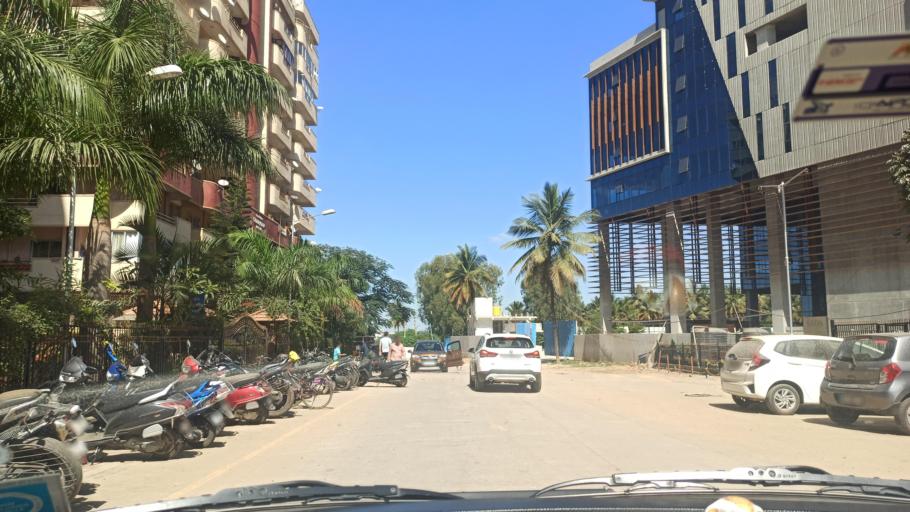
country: IN
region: Karnataka
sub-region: Bangalore Urban
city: Bangalore
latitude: 12.9262
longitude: 77.6654
